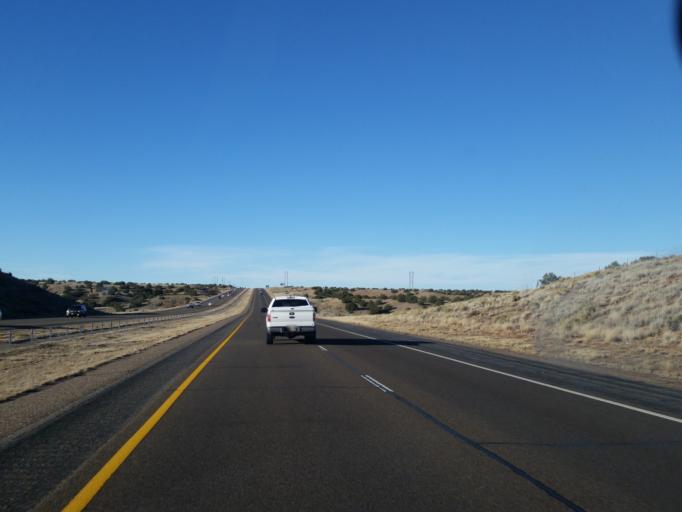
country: US
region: New Mexico
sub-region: Sandoval County
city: Santo Domingo Pueblo
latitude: 35.4848
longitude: -106.2694
